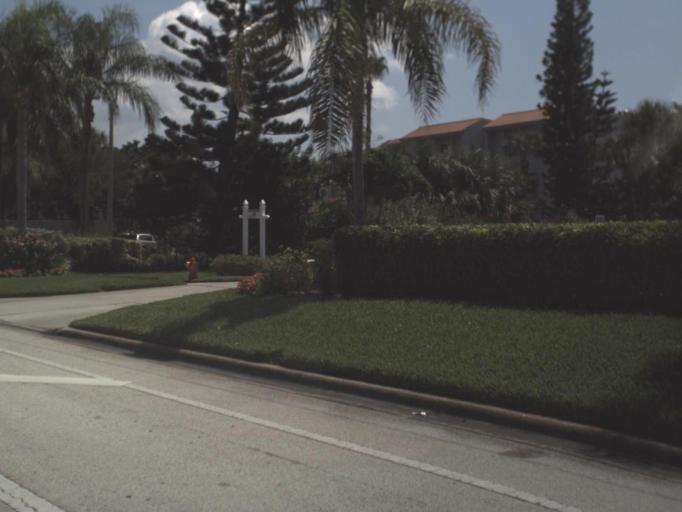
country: US
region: Florida
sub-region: Pinellas County
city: Tierra Verde
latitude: 27.6827
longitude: -82.7245
